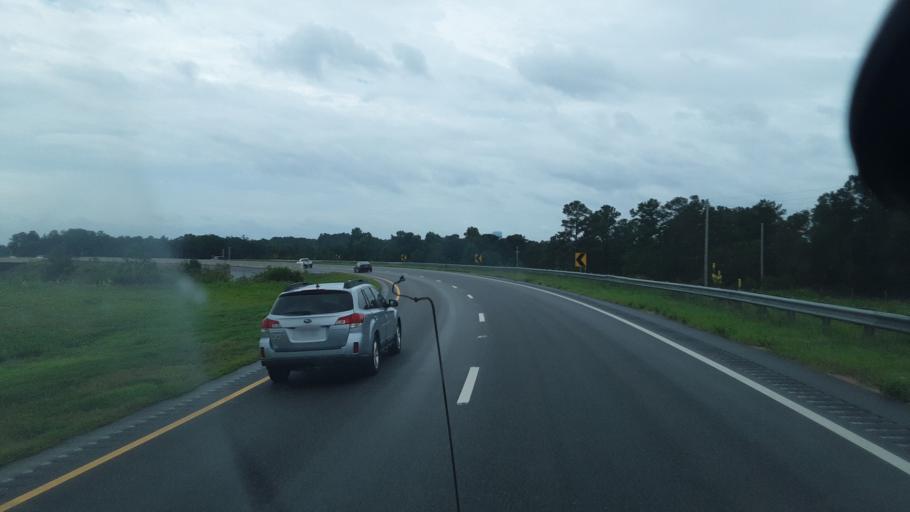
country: US
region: North Carolina
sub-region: Richmond County
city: Rockingham
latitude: 34.9996
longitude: -79.7794
